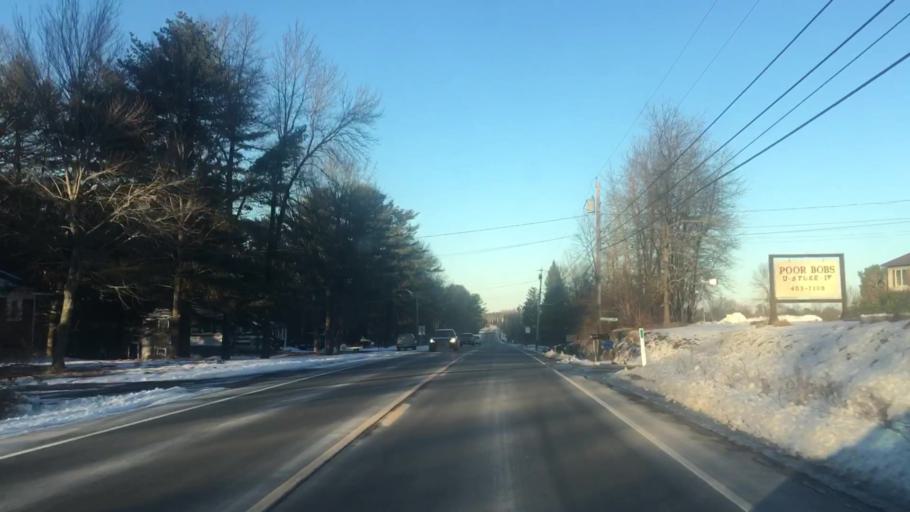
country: US
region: Maine
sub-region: Kennebec County
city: Benton
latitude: 44.5876
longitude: -69.5449
